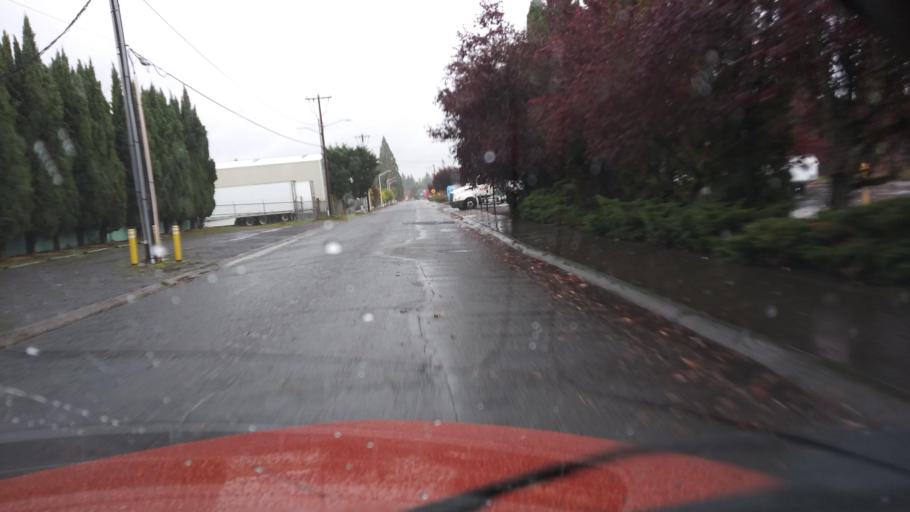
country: US
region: Oregon
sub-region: Washington County
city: Cornelius
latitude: 45.5218
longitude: -123.0398
